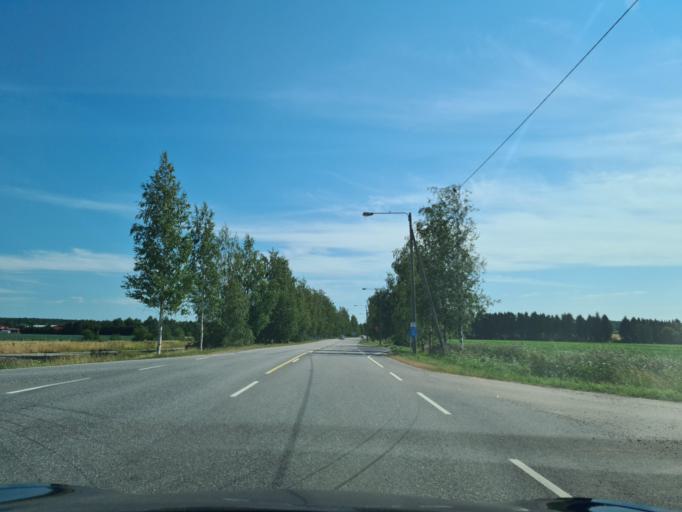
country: FI
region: Varsinais-Suomi
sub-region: Turku
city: Paimio
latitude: 60.4546
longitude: 22.6654
